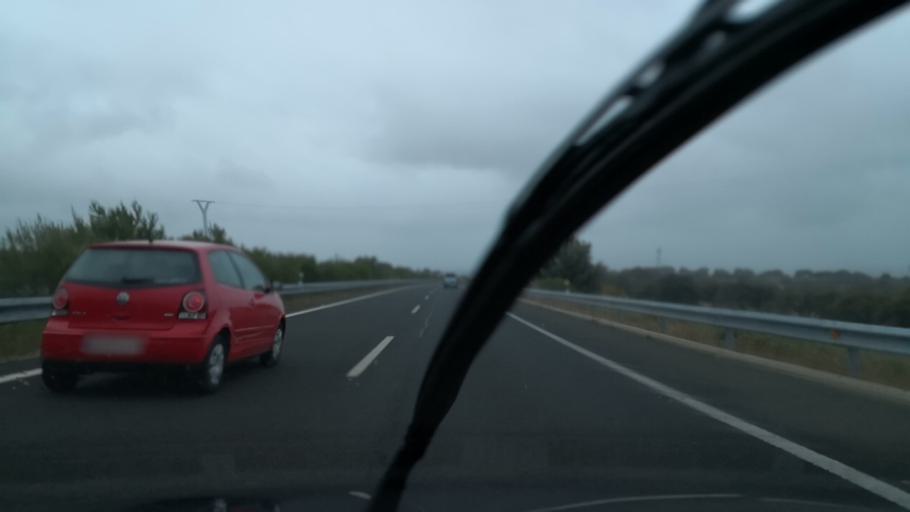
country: ES
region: Extremadura
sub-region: Provincia de Caceres
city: Santiago del Campo
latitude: 39.6405
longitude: -6.3942
